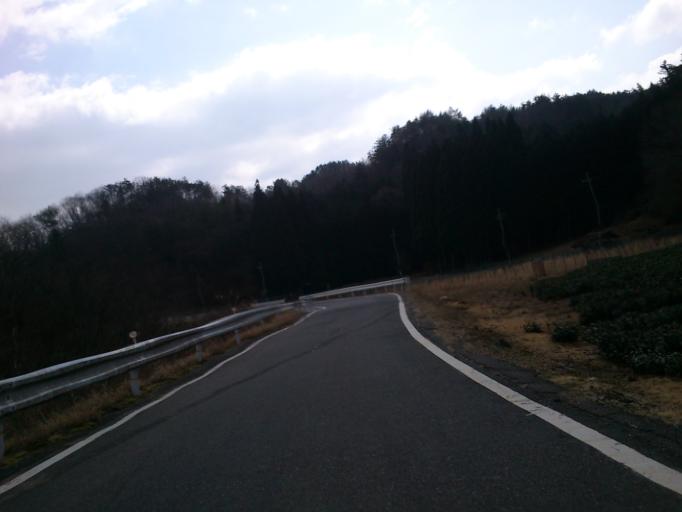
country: JP
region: Mie
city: Ueno-ebisumachi
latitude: 34.8305
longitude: 135.9860
